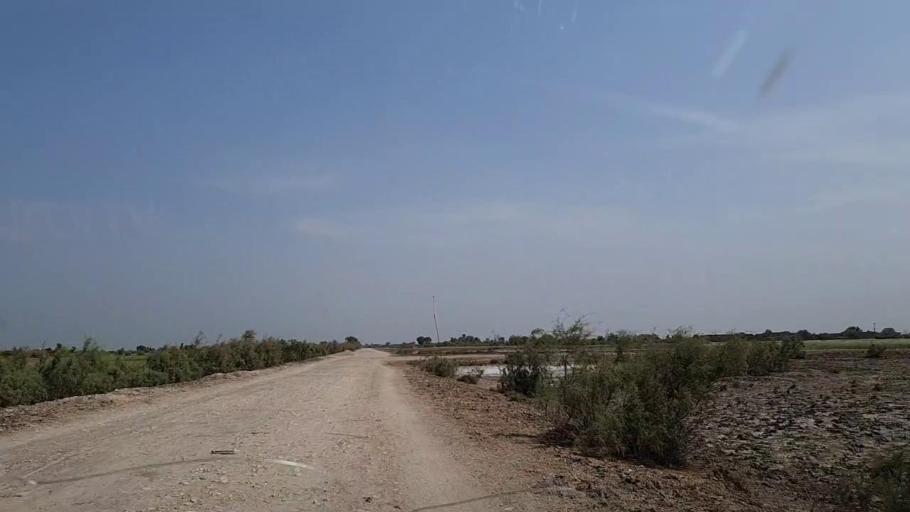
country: PK
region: Sindh
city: Khanpur
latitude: 27.8085
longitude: 69.3094
